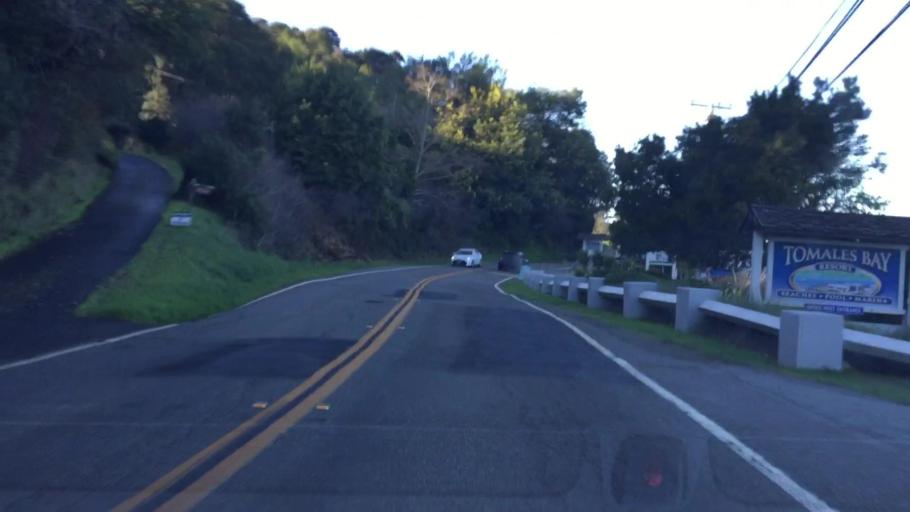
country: US
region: California
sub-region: Marin County
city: Inverness
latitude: 38.1065
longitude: -122.8625
